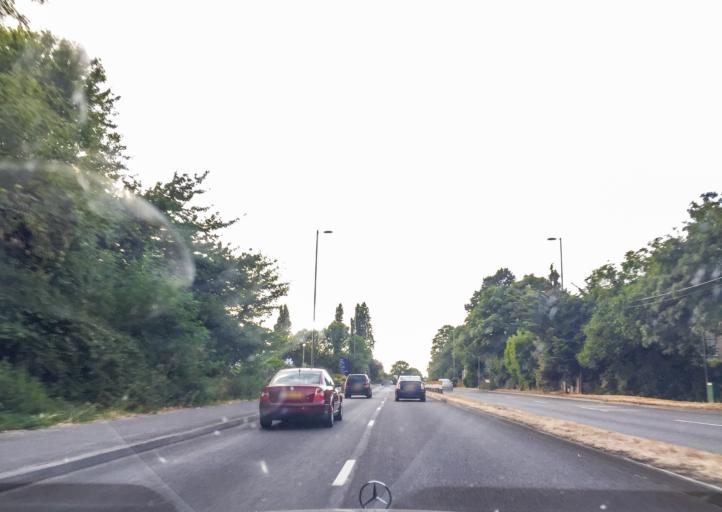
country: GB
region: England
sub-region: Surrey
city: Staines
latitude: 51.4588
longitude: -0.4939
